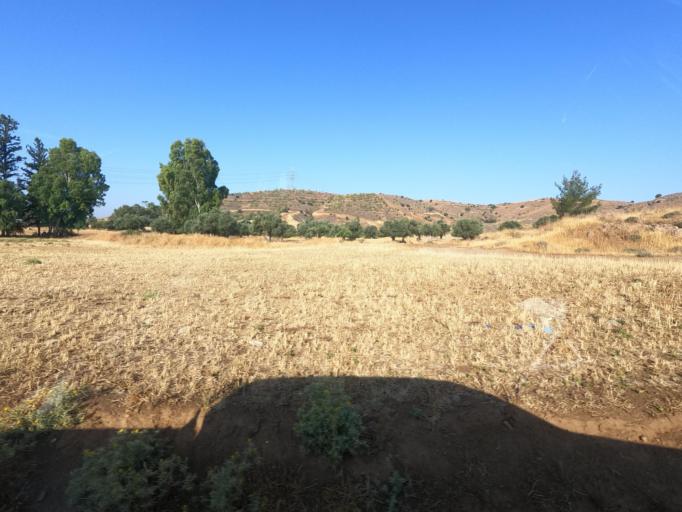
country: CY
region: Lefkosia
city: Lympia
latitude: 34.9880
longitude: 33.4371
